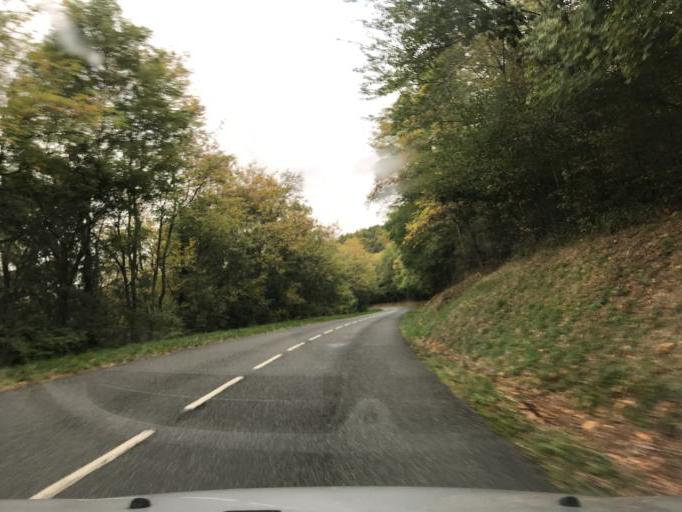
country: FR
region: Rhone-Alpes
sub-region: Departement du Rhone
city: Le Perreon
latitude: 46.0171
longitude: 4.5756
